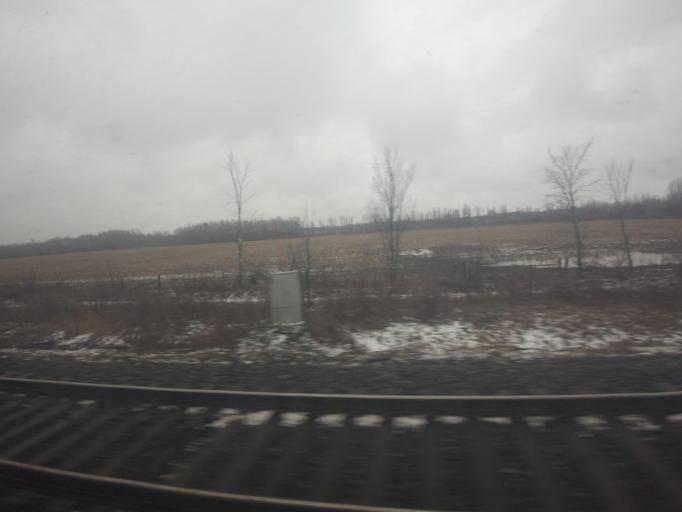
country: CA
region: Ontario
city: Deseronto
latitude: 44.2151
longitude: -77.1753
